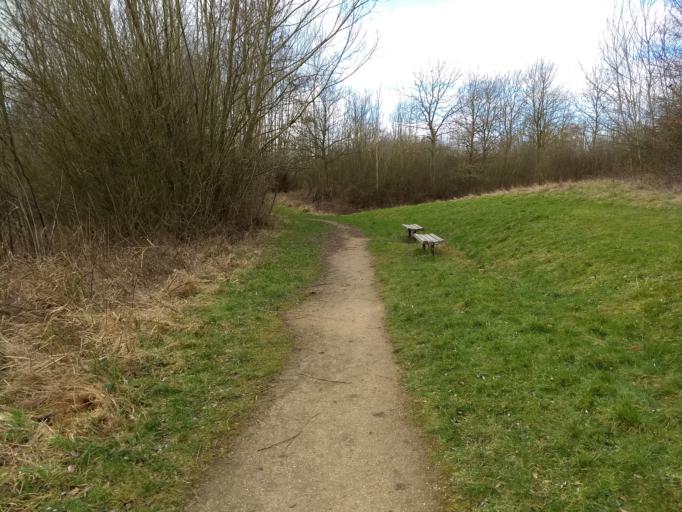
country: GB
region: England
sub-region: Buckinghamshire
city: Bletchley
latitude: 51.9845
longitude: -0.7350
